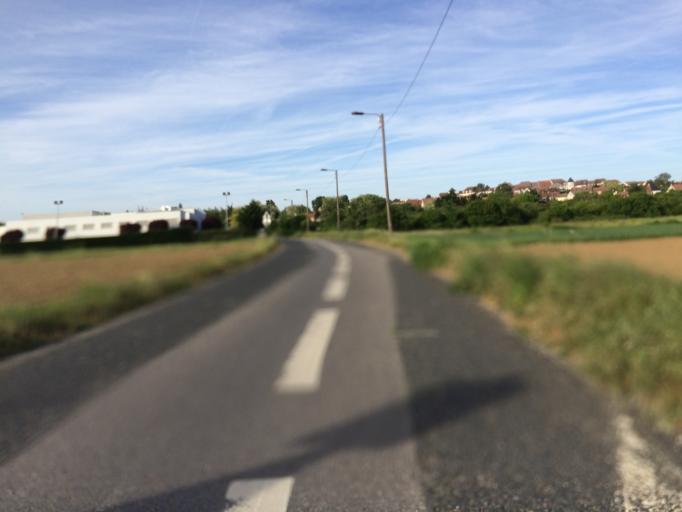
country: FR
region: Ile-de-France
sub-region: Departement de l'Essonne
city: Montlhery
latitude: 48.6441
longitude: 2.2759
